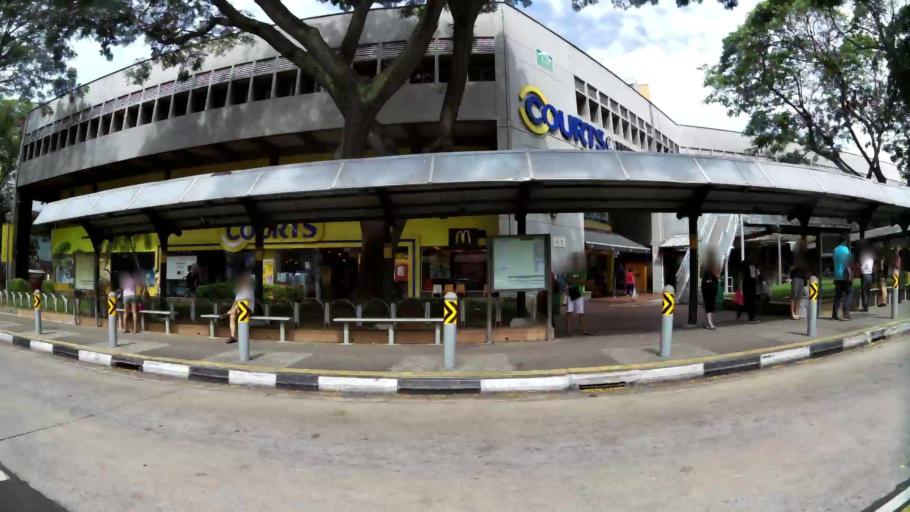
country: SG
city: Singapore
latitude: 1.3124
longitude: 103.7658
